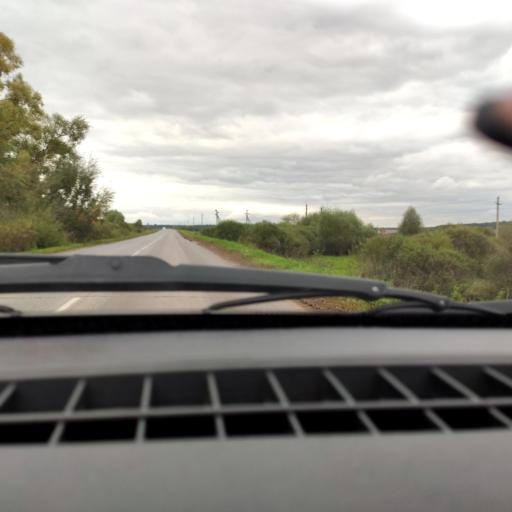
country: RU
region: Bashkortostan
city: Iglino
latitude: 54.7425
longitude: 56.3975
